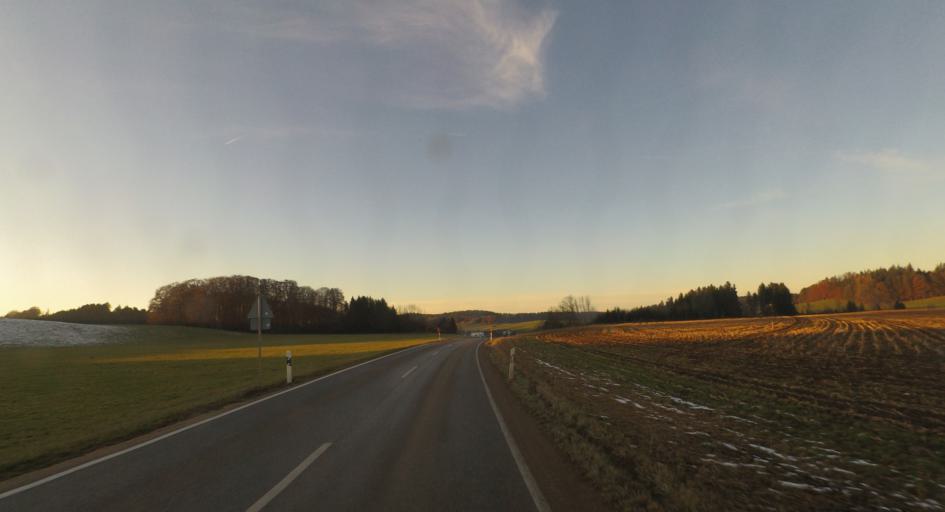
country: DE
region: Bavaria
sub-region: Upper Bavaria
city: Nussdorf
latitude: 47.8845
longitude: 12.5979
